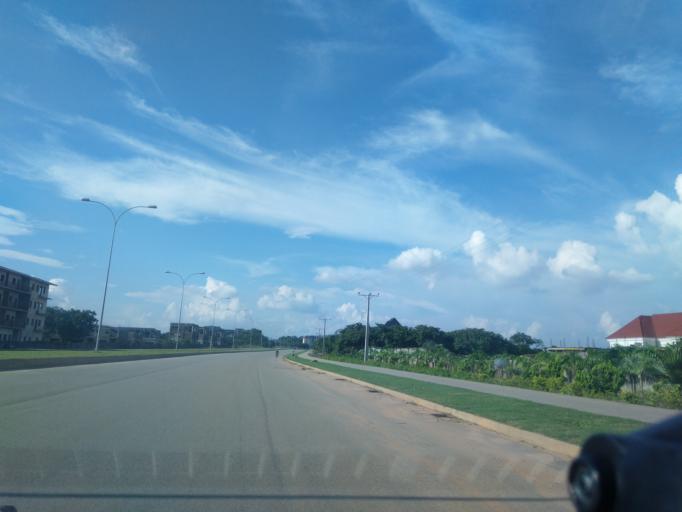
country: NG
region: Abuja Federal Capital Territory
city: Abuja
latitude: 9.0524
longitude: 7.3900
